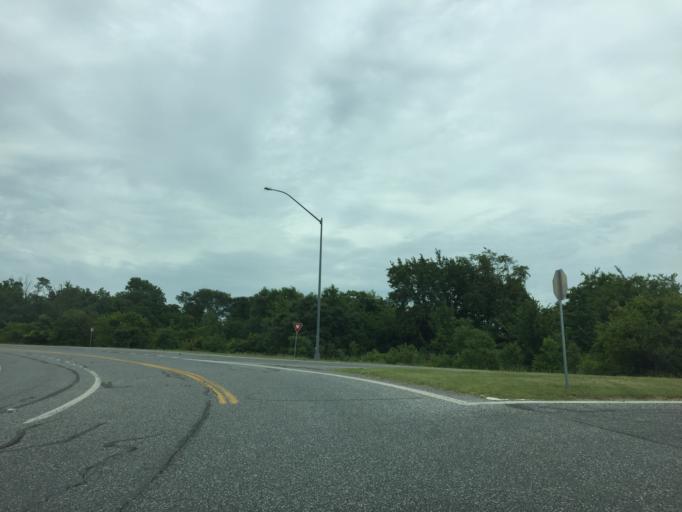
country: US
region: Maryland
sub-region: Baltimore County
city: Edgemere
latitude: 39.2303
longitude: -76.4646
